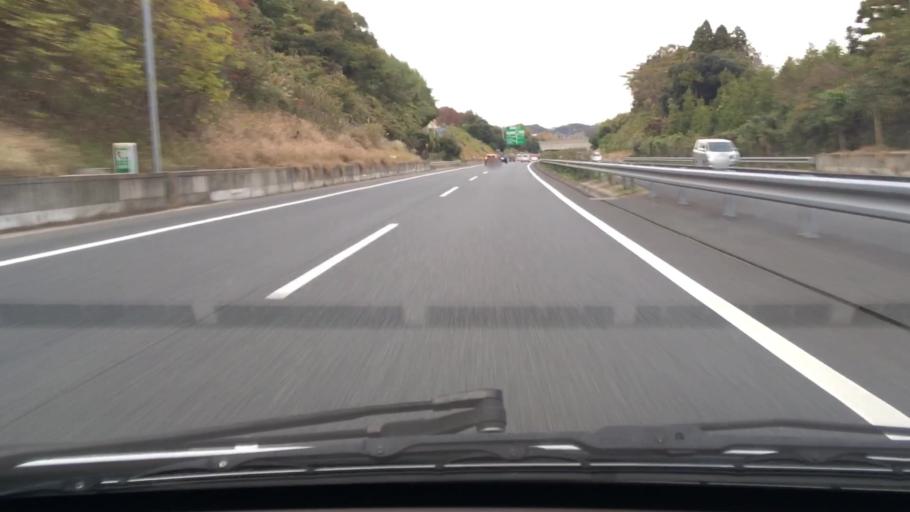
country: JP
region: Chiba
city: Kisarazu
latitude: 35.3362
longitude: 139.9447
